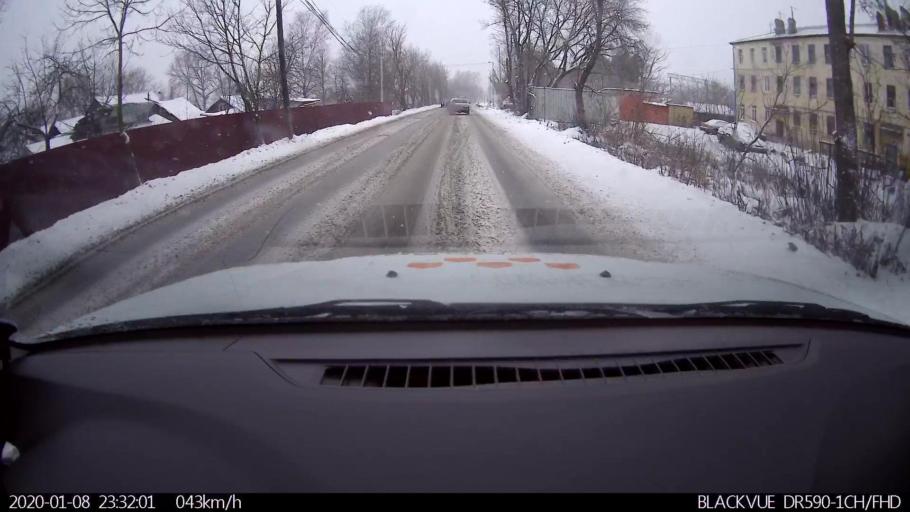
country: RU
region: Nizjnij Novgorod
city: Gorbatovka
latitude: 56.2635
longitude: 43.7488
